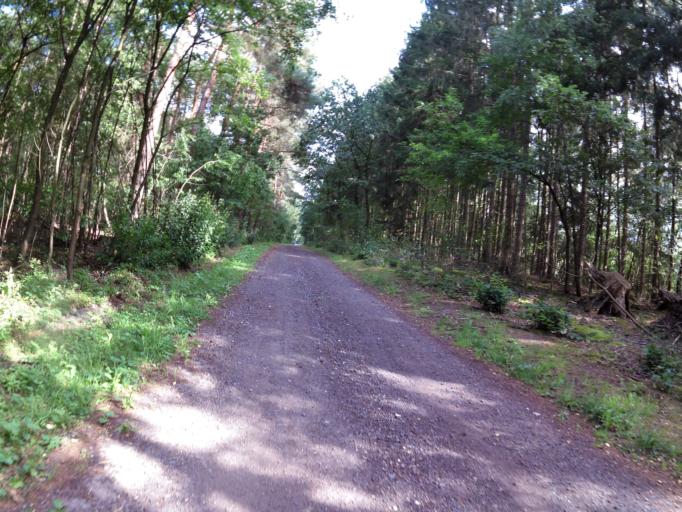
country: DE
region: Lower Saxony
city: Heeslingen
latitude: 53.2955
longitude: 9.3841
